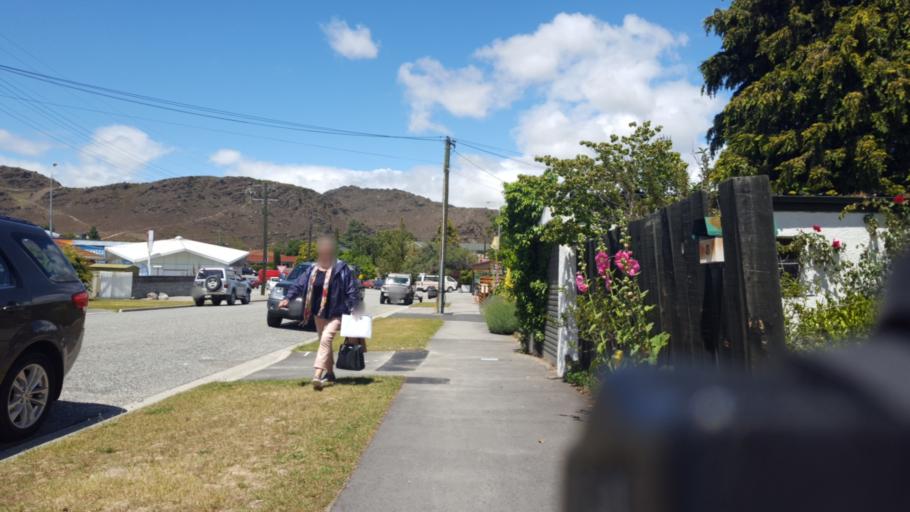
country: NZ
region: Otago
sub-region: Queenstown-Lakes District
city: Wanaka
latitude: -45.2518
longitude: 169.3945
